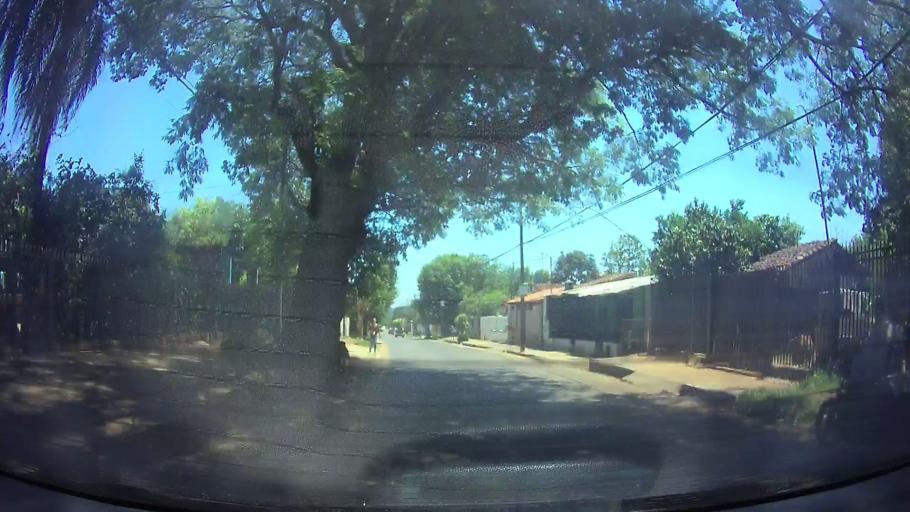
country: PY
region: Central
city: San Lorenzo
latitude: -25.3351
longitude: -57.4850
